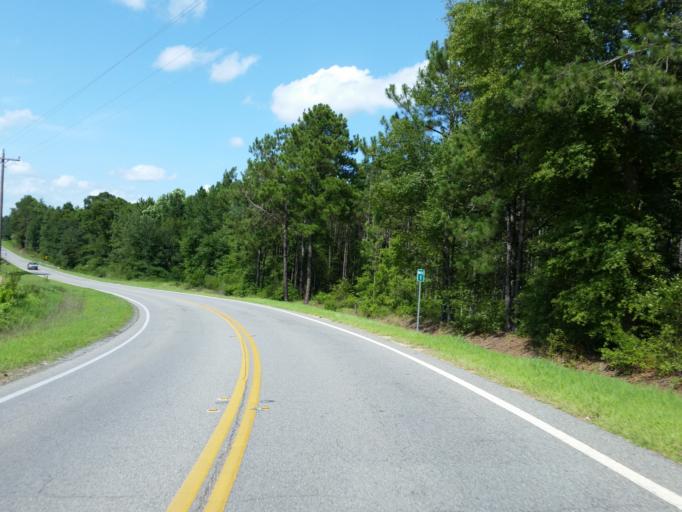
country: US
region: Georgia
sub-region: Tift County
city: Tifton
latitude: 31.5814
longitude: -83.4809
